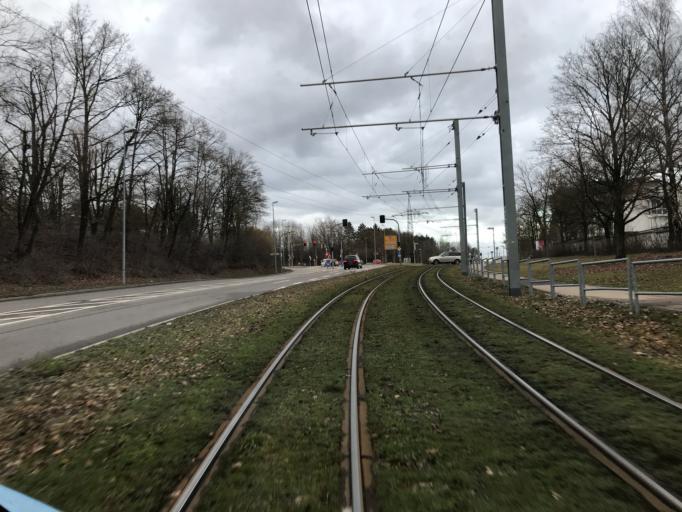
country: DE
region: Bavaria
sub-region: Swabia
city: Neu-Ulm
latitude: 48.4244
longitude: 10.0122
